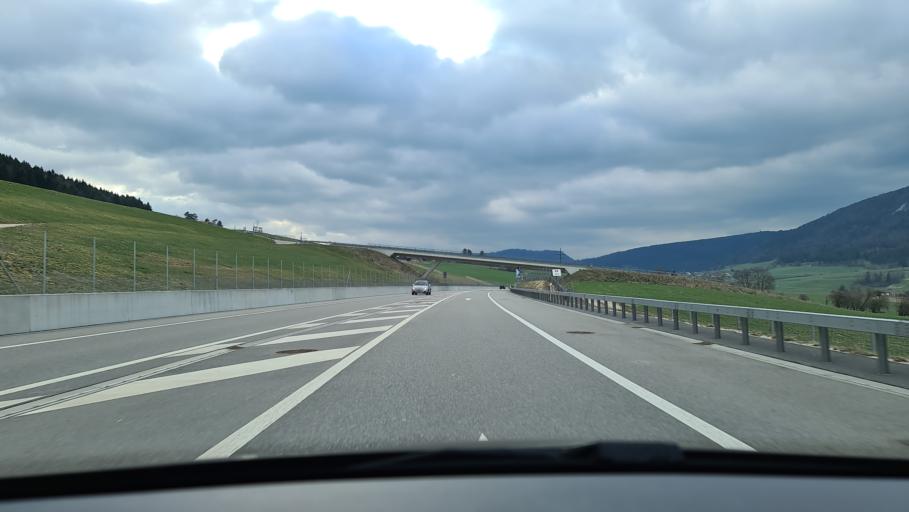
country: CH
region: Bern
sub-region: Jura bernois
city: Malleray
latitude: 47.2307
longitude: 7.2709
